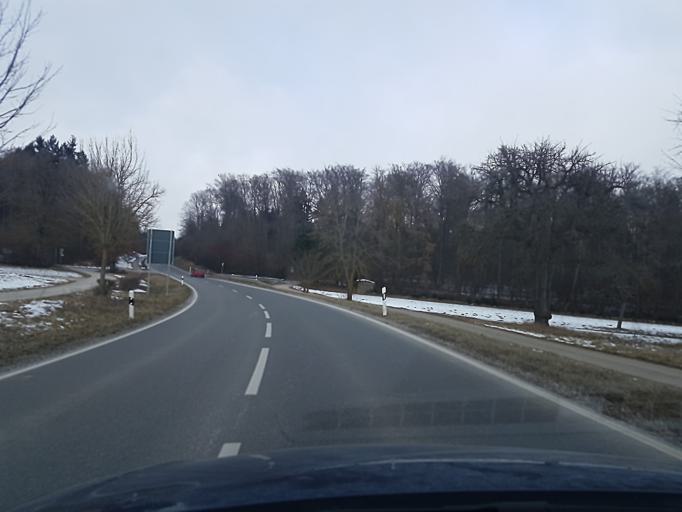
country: DE
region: Baden-Wuerttemberg
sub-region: Regierungsbezirk Stuttgart
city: Renningen
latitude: 48.7830
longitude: 8.9312
